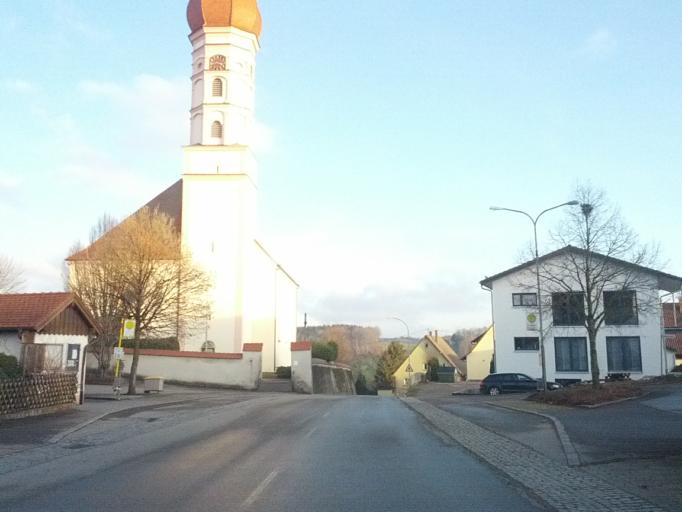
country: DE
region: Baden-Wuerttemberg
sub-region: Tuebingen Region
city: Steinhausen an der Rottum
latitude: 48.0237
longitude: 9.9550
